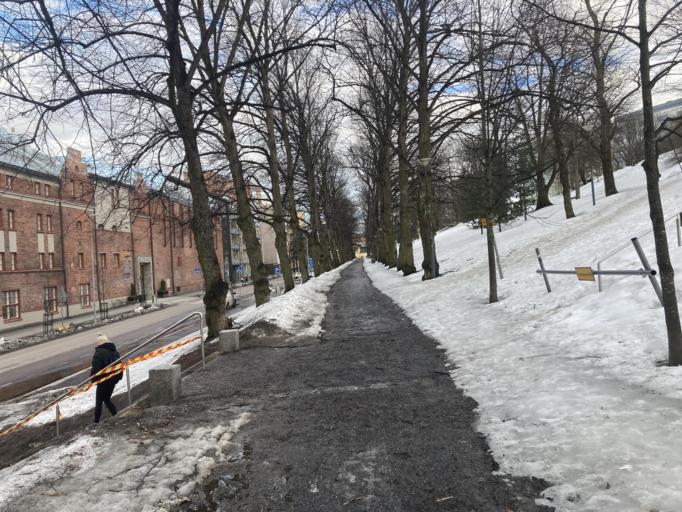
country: FI
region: Paijanne Tavastia
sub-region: Lahti
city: Lahti
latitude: 60.9862
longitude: 25.6576
